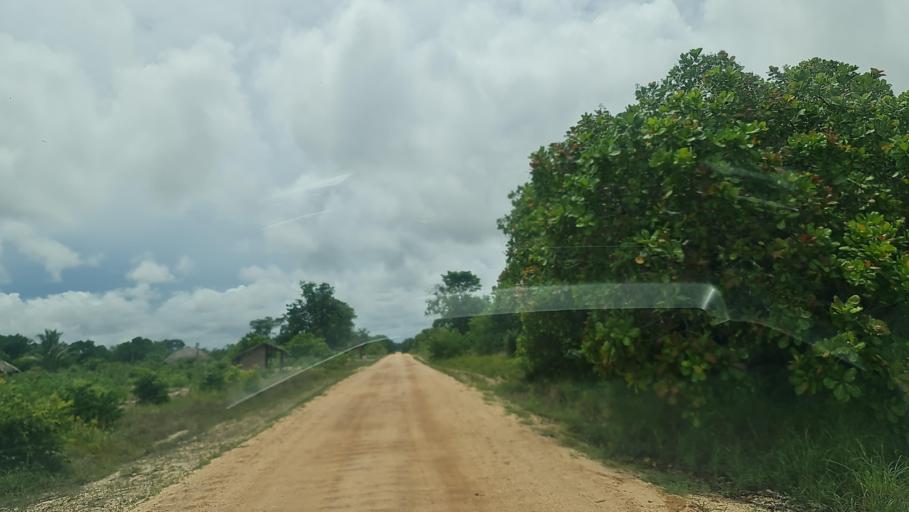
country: MZ
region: Zambezia
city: Quelimane
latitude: -17.2611
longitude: 37.2338
